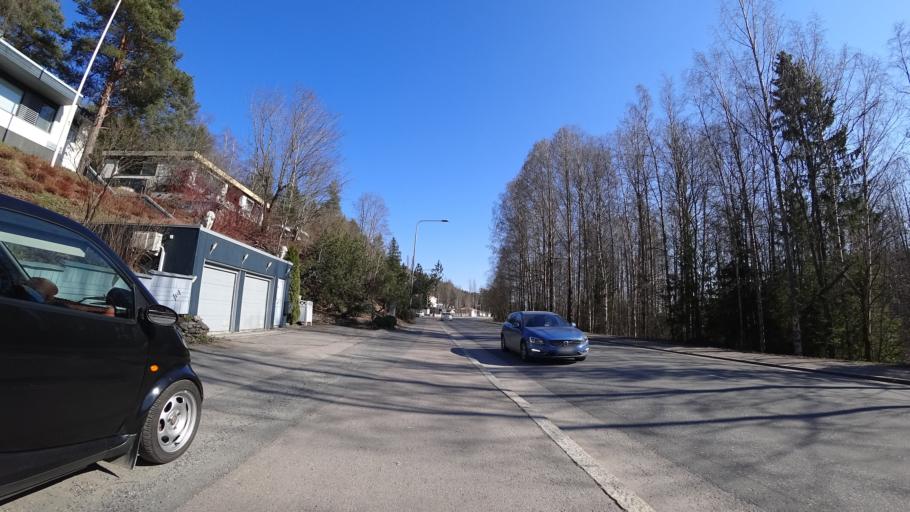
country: FI
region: Pirkanmaa
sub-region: Tampere
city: Pirkkala
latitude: 61.5179
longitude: 23.6467
